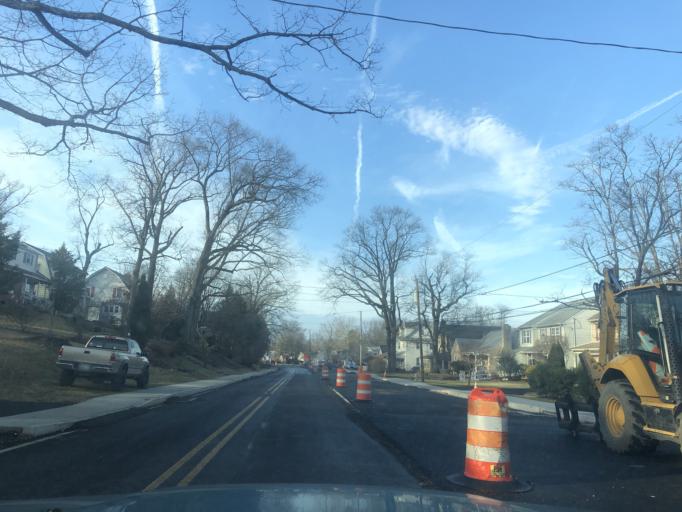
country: US
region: Pennsylvania
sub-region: Montgomery County
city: Glenside
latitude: 40.1169
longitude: -75.1472
